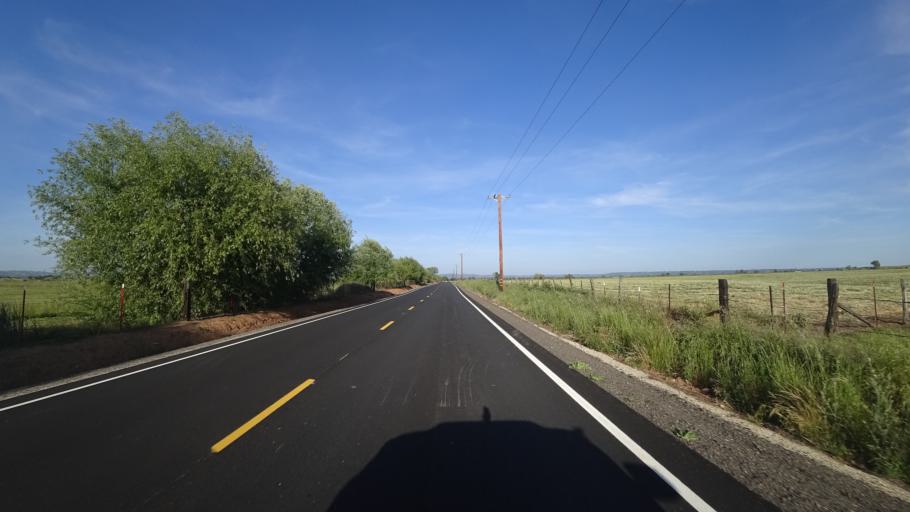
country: US
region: California
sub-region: Placer County
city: Lincoln
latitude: 38.9265
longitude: -121.3087
